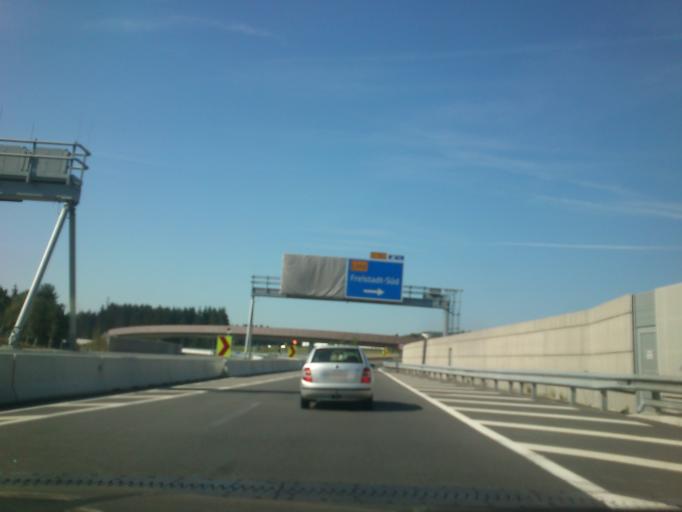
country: AT
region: Upper Austria
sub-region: Politischer Bezirk Freistadt
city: Freistadt
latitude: 48.4841
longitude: 14.5021
